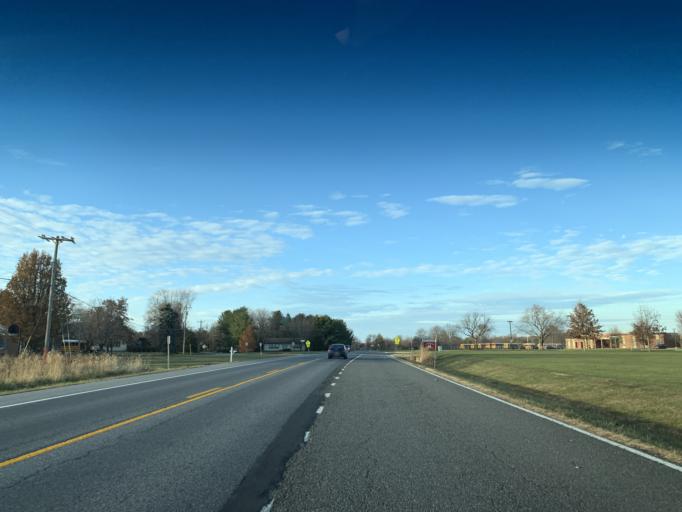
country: US
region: Maryland
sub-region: Kent County
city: Chestertown
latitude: 39.2813
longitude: -76.0942
